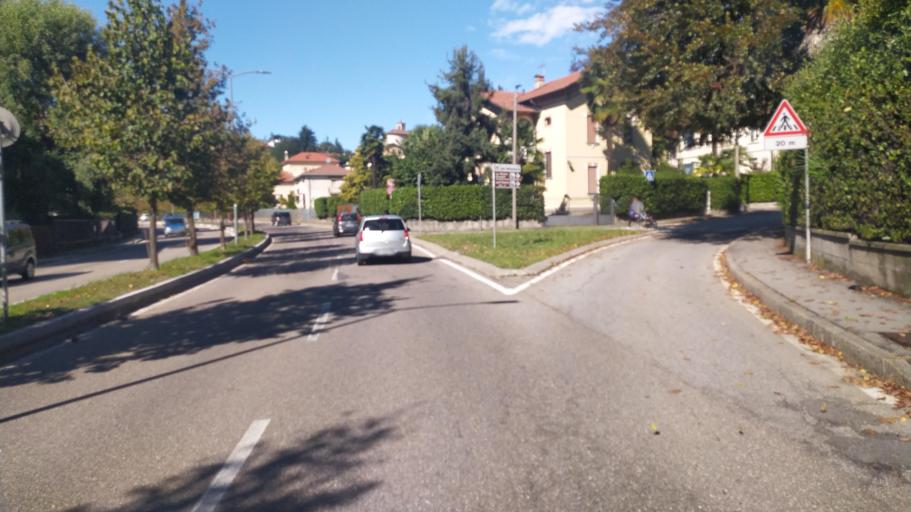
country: IT
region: Lombardy
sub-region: Provincia di Varese
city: Varese
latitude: 45.8093
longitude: 8.8306
